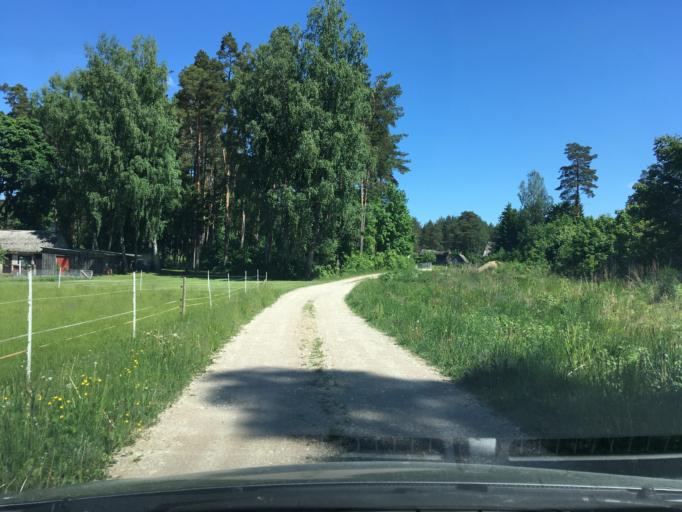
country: EE
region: Harju
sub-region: Raasiku vald
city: Raasiku
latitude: 59.1628
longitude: 25.1638
